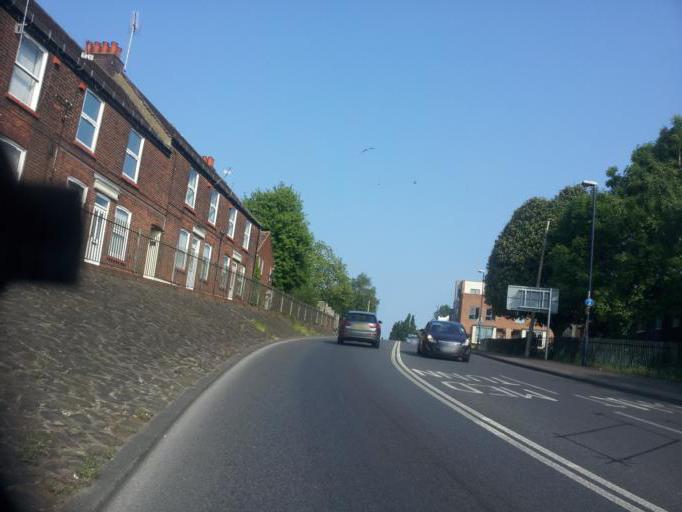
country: GB
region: England
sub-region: Kent
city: Chatham
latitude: 51.3930
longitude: 0.5301
